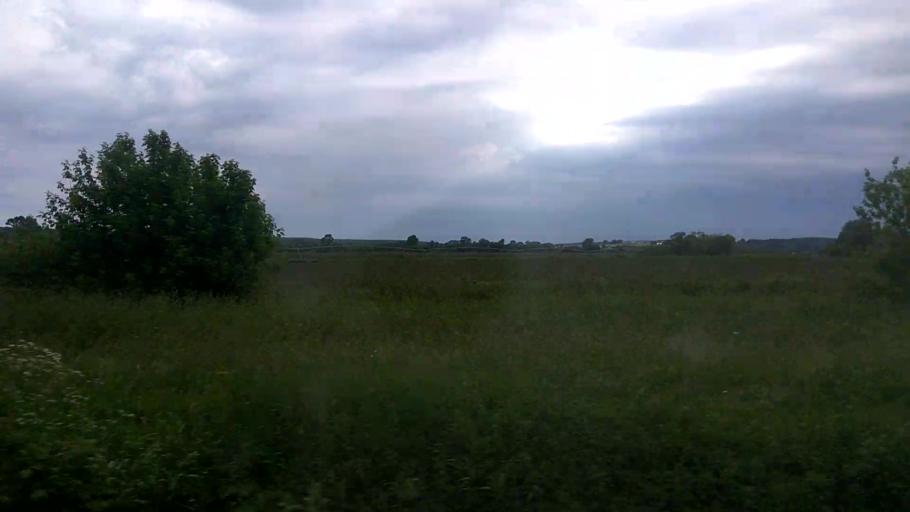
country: RU
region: Moskovskaya
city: Ozery
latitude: 54.8398
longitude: 38.5773
